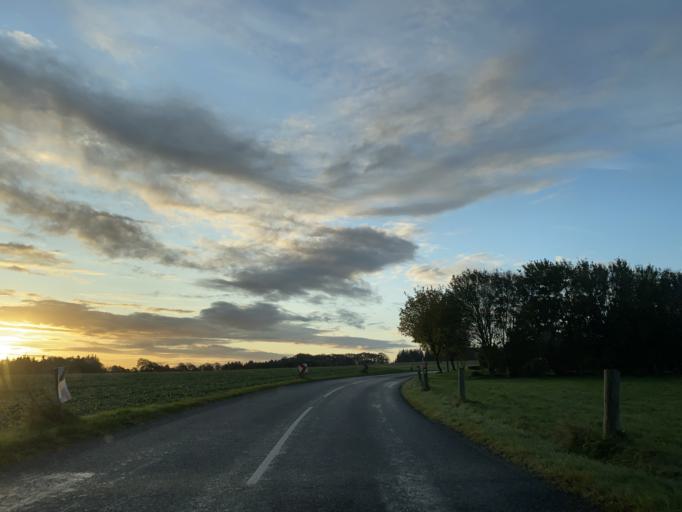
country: DK
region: Central Jutland
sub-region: Skanderborg Kommune
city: Ry
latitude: 56.2068
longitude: 9.7536
